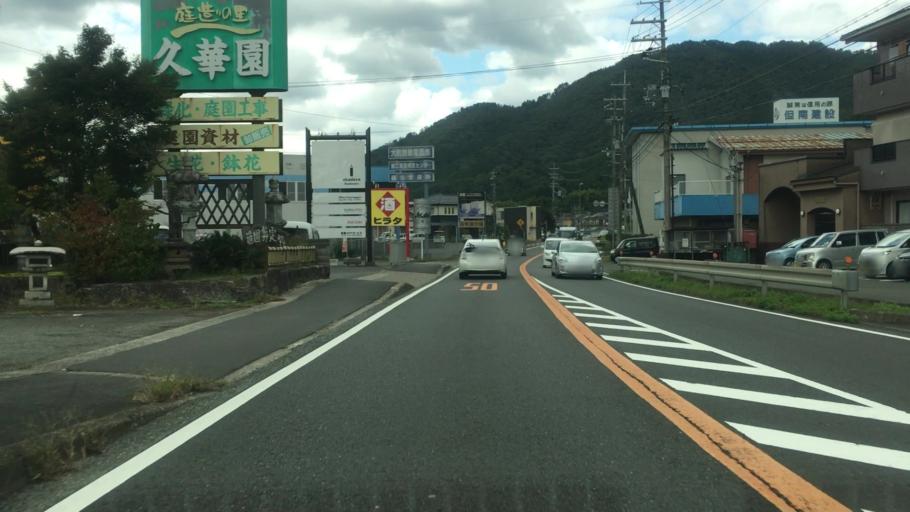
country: JP
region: Hyogo
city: Toyooka
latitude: 35.3220
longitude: 134.8786
